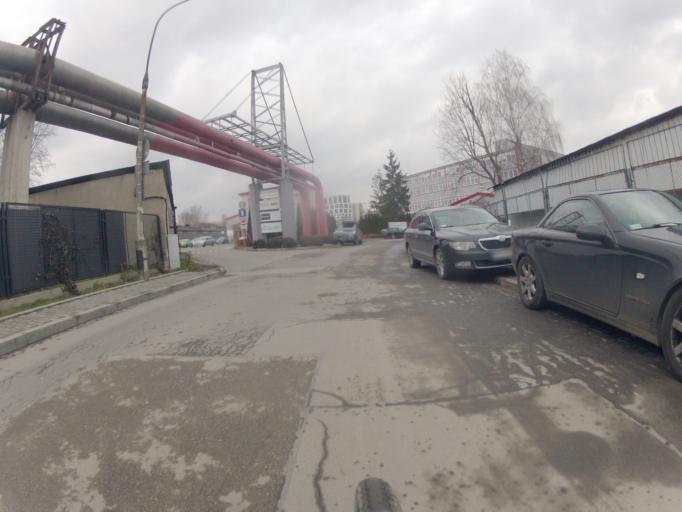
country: PL
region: Lesser Poland Voivodeship
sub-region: Krakow
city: Krakow
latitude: 50.0649
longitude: 19.9744
